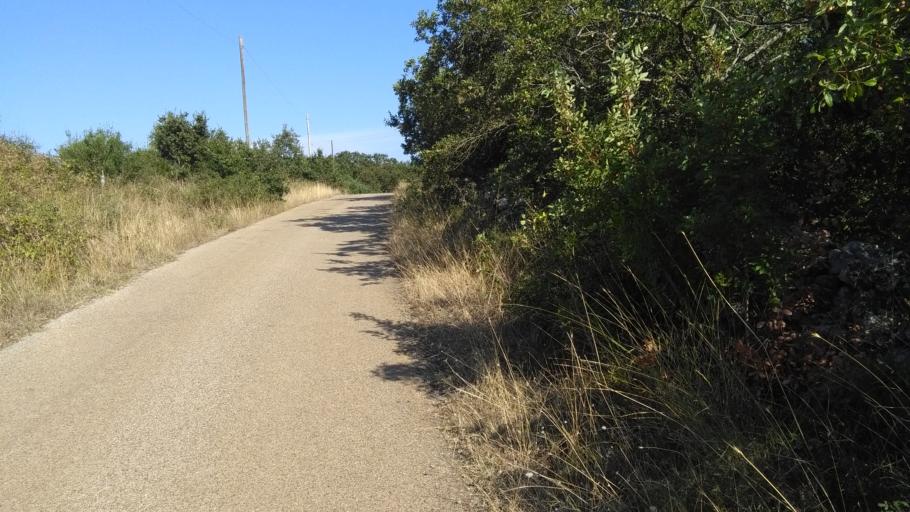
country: IT
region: Apulia
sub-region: Provincia di Bari
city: Putignano
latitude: 40.8199
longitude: 17.0478
